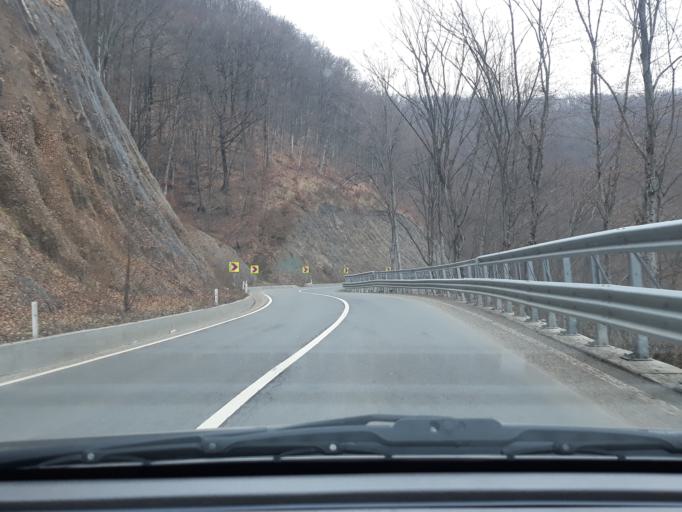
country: RO
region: Bihor
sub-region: Oras Alesd
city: Pestis
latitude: 47.1099
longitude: 22.4057
